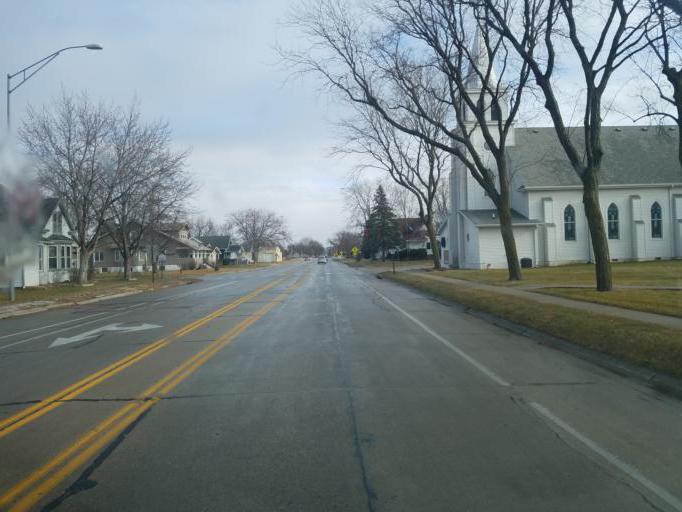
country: US
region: Nebraska
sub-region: Pierce County
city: Pierce
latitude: 42.1963
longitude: -97.5281
